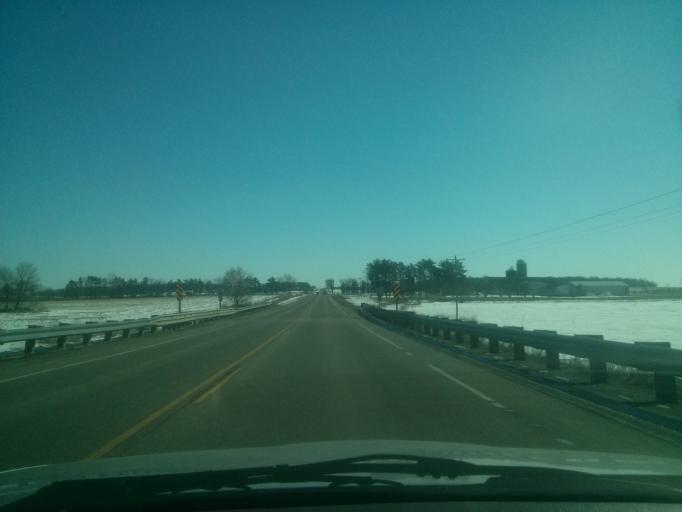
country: US
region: Wisconsin
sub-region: Saint Croix County
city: New Richmond
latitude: 45.1370
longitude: -92.4583
